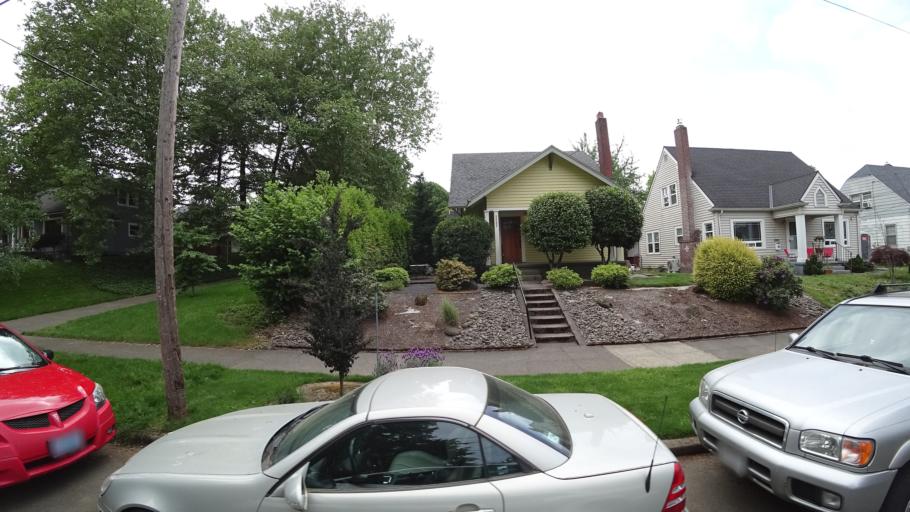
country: US
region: Oregon
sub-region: Multnomah County
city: Portland
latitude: 45.5469
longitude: -122.6535
